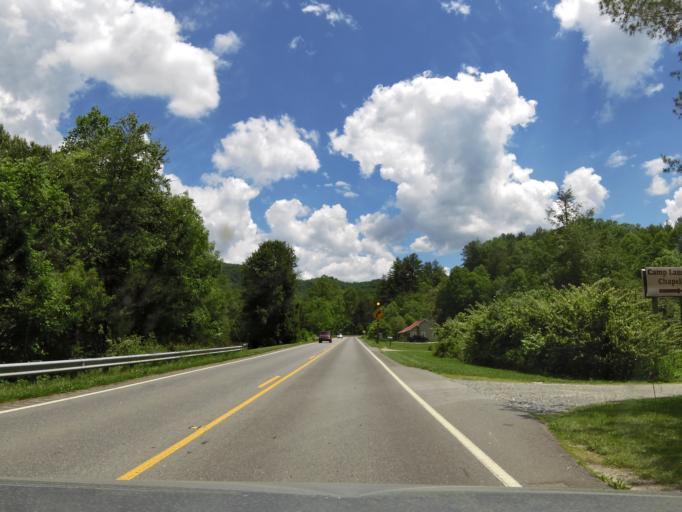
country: US
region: North Carolina
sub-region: Graham County
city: Robbinsville
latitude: 35.2885
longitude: -83.7700
